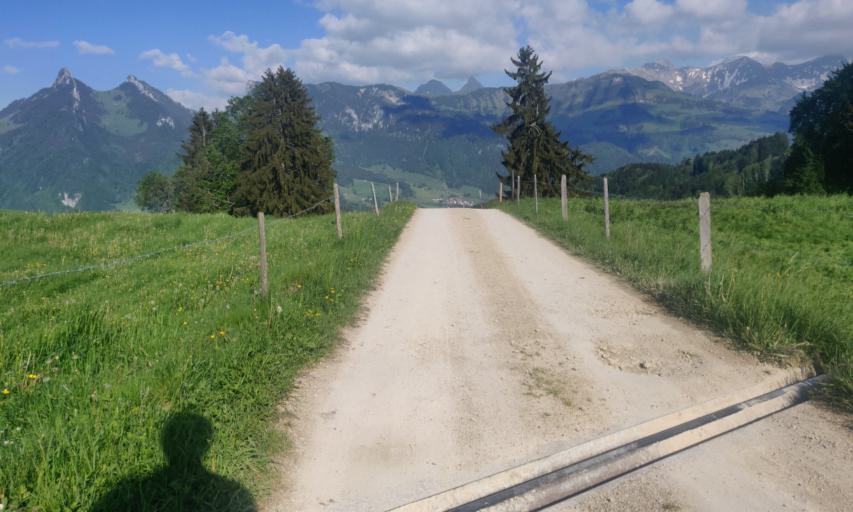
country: CH
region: Fribourg
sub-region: Gruyere District
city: Gruyeres
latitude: 46.5780
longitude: 7.0516
